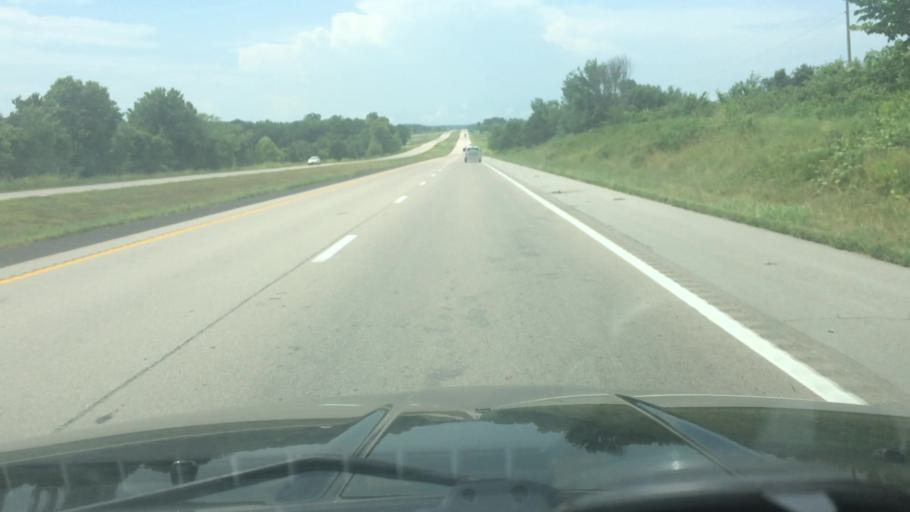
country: US
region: Missouri
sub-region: Polk County
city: Humansville
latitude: 37.7832
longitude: -93.5778
